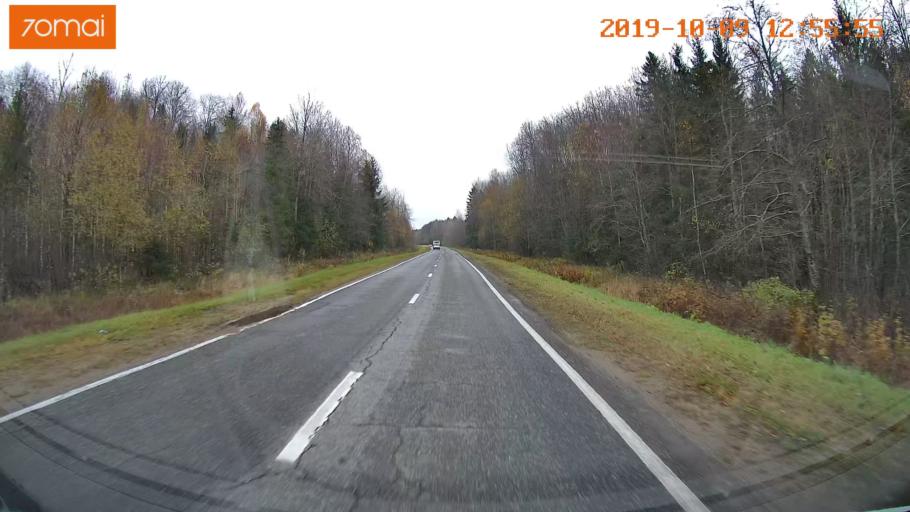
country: RU
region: Jaroslavl
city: Prechistoye
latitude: 58.3967
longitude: 40.4054
